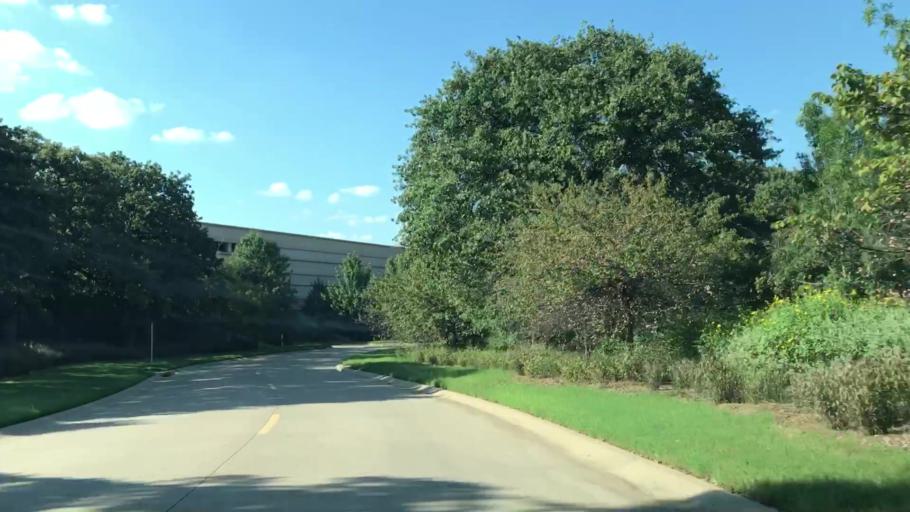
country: US
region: Texas
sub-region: Denton County
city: Trophy Club
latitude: 32.9835
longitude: -97.1859
